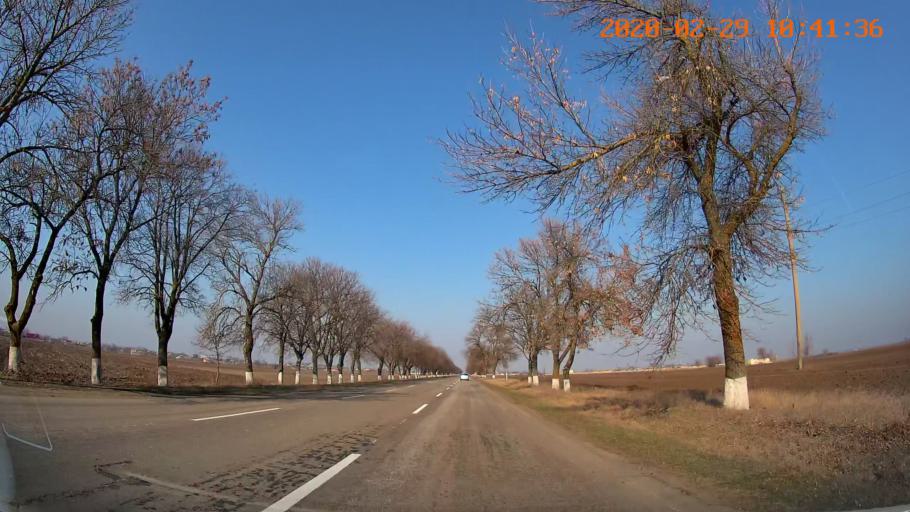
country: MD
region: Telenesti
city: Grigoriopol
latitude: 47.0439
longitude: 29.4228
